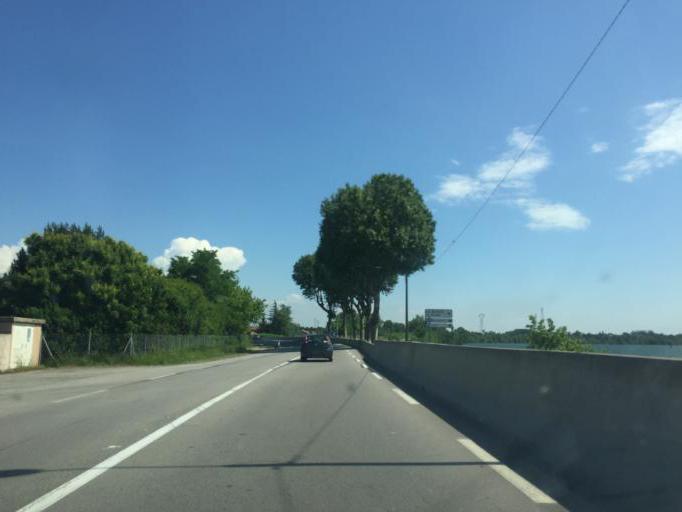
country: FR
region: Rhone-Alpes
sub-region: Departement de l'Ardeche
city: Tournon-sur-Rhone
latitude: 45.0609
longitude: 4.8602
